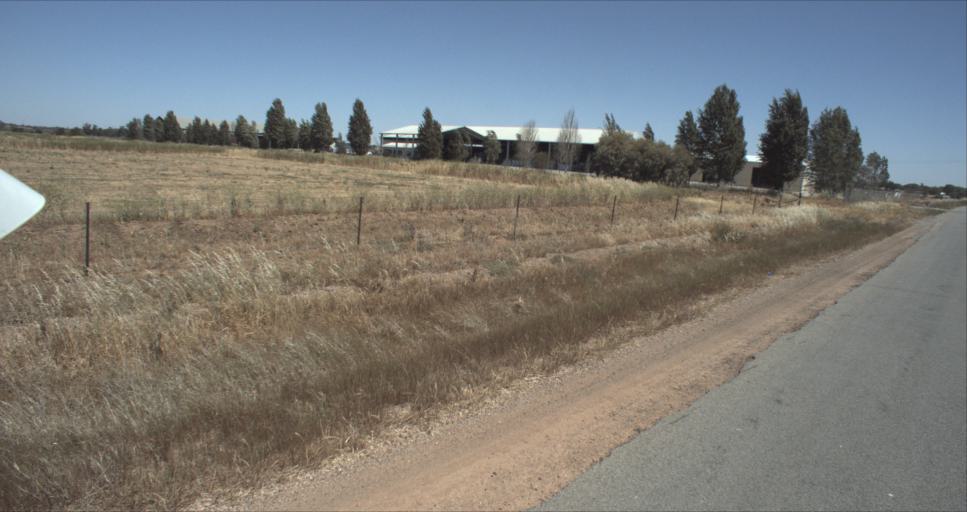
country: AU
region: New South Wales
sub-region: Leeton
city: Leeton
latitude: -34.5435
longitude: 146.4301
